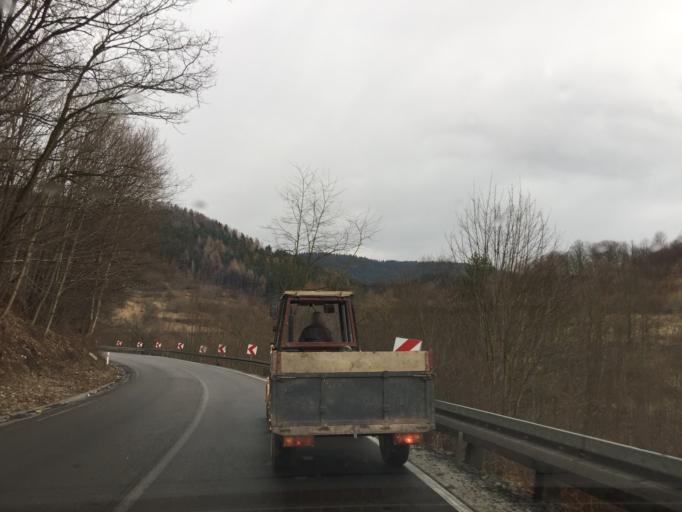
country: PL
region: Lesser Poland Voivodeship
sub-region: Powiat myslenicki
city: Harbutowice
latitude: 49.8051
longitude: 19.7664
